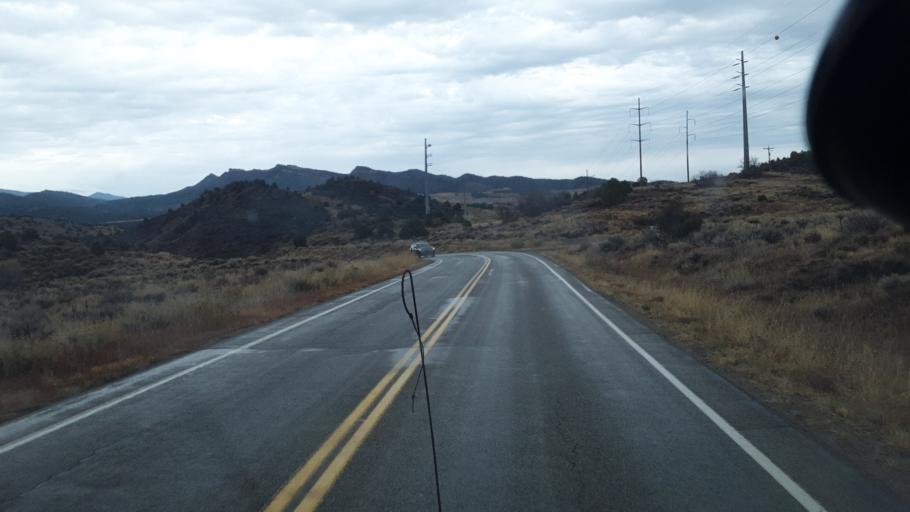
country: US
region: Colorado
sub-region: La Plata County
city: Durango
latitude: 37.2444
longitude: -107.8949
